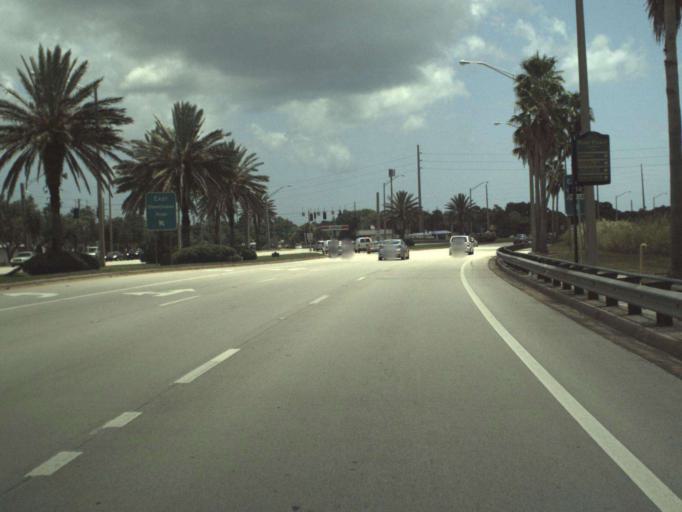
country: US
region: Florida
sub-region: Saint Lucie County
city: Fort Pierce South
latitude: 27.4246
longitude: -80.3692
